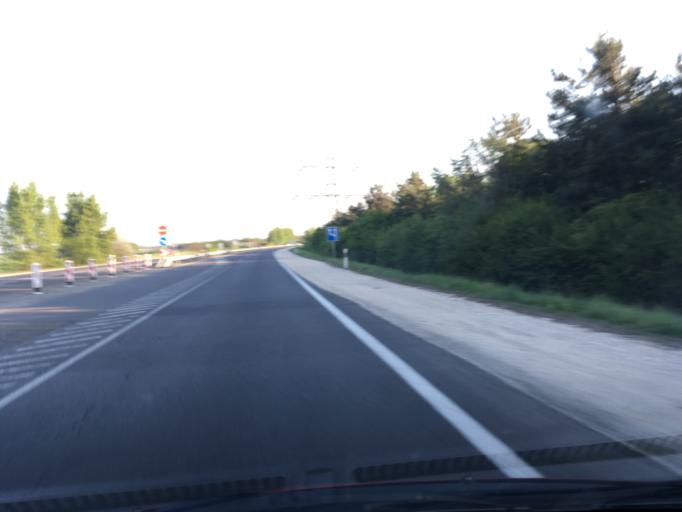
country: HU
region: Pest
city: Szod
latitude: 47.6892
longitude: 19.1741
